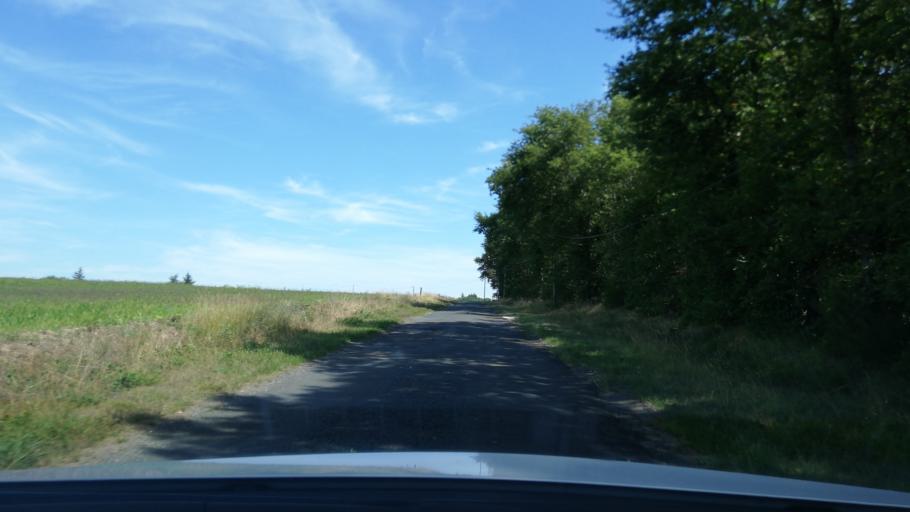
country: FR
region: Centre
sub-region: Departement d'Indre-et-Loire
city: Mazieres-de-Touraine
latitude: 47.3934
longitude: 0.4310
